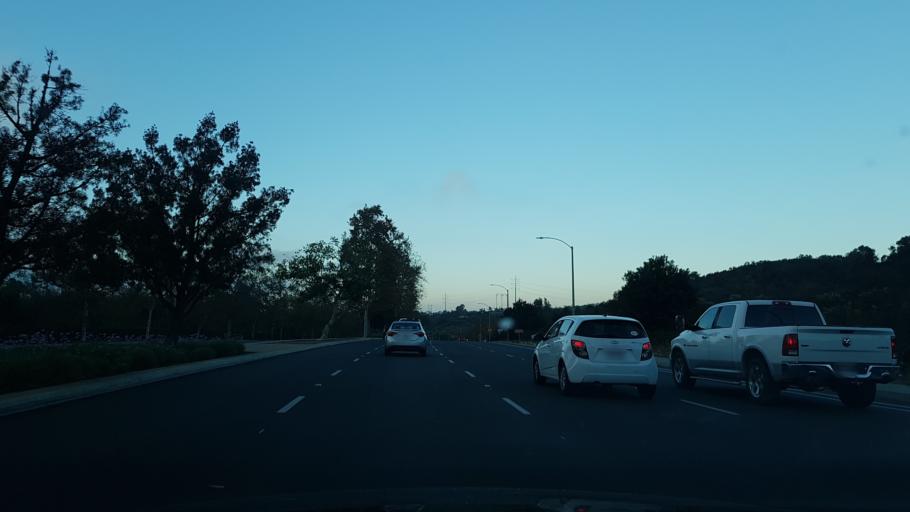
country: US
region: California
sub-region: San Diego County
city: Encinitas
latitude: 33.0620
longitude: -117.2627
